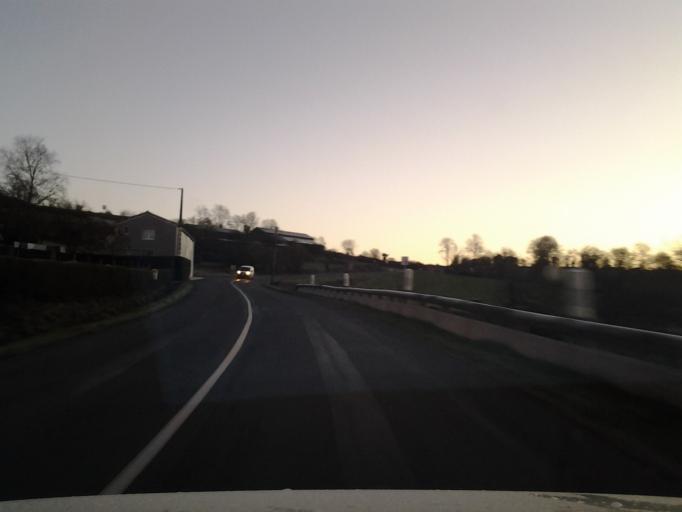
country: FR
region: Pays de la Loire
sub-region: Departement de la Vendee
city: Les Epesses
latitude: 46.8748
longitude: -0.9323
